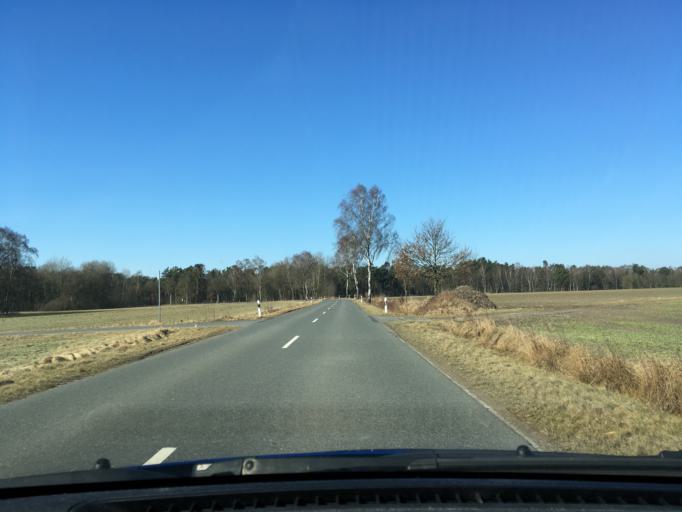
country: DE
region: Lower Saxony
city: Schneverdingen
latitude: 53.0832
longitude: 9.8426
